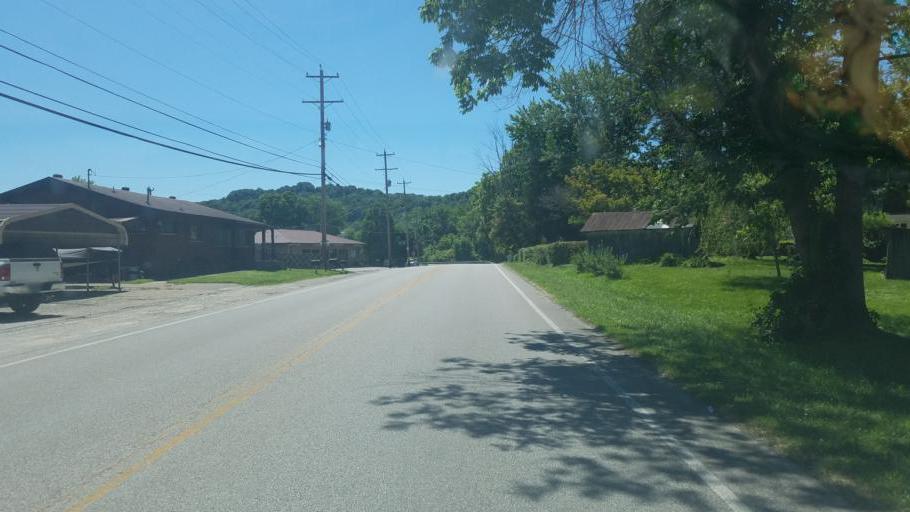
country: US
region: West Virginia
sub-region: Cabell County
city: Pea Ridge
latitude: 38.4423
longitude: -82.3548
